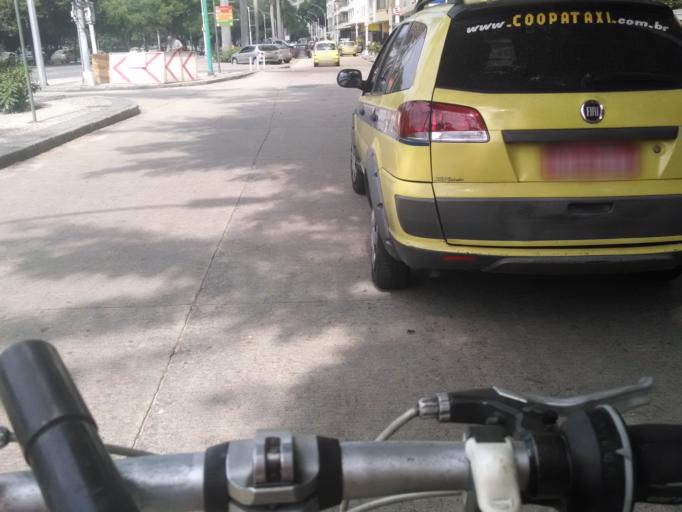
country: BR
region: Rio de Janeiro
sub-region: Rio De Janeiro
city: Rio de Janeiro
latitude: -22.9299
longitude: -43.1744
